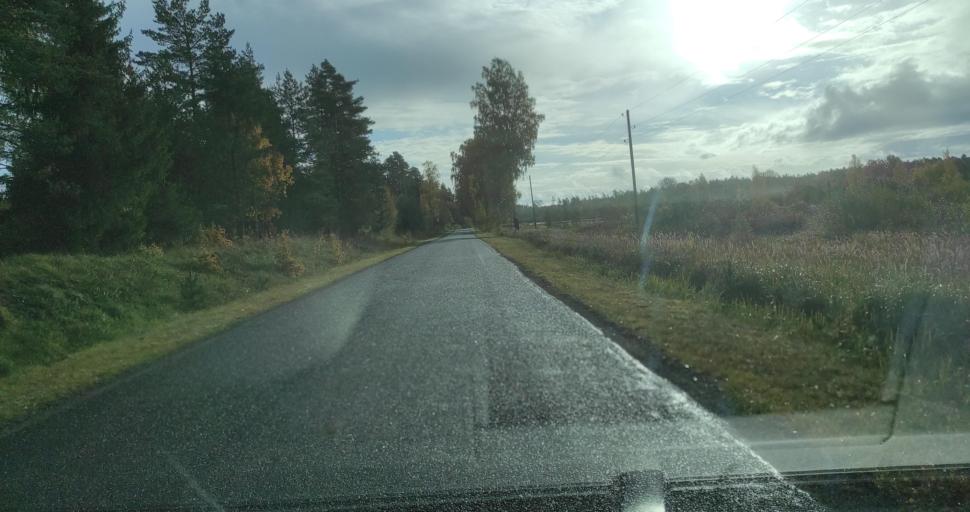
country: LV
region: Skrunda
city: Skrunda
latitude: 56.6840
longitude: 22.0631
